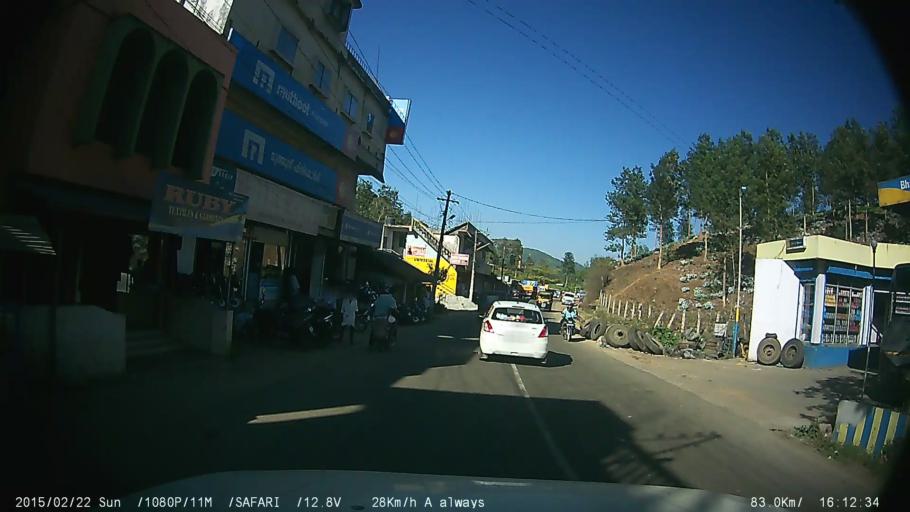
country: IN
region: Tamil Nadu
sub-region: Theni
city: Gudalur
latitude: 9.5747
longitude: 77.0932
